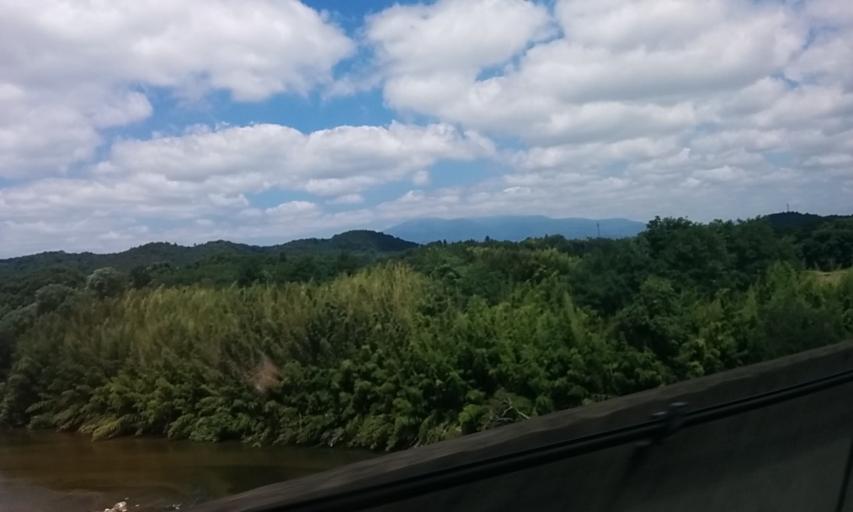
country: JP
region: Fukushima
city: Motomiya
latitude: 37.4638
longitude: 140.4112
